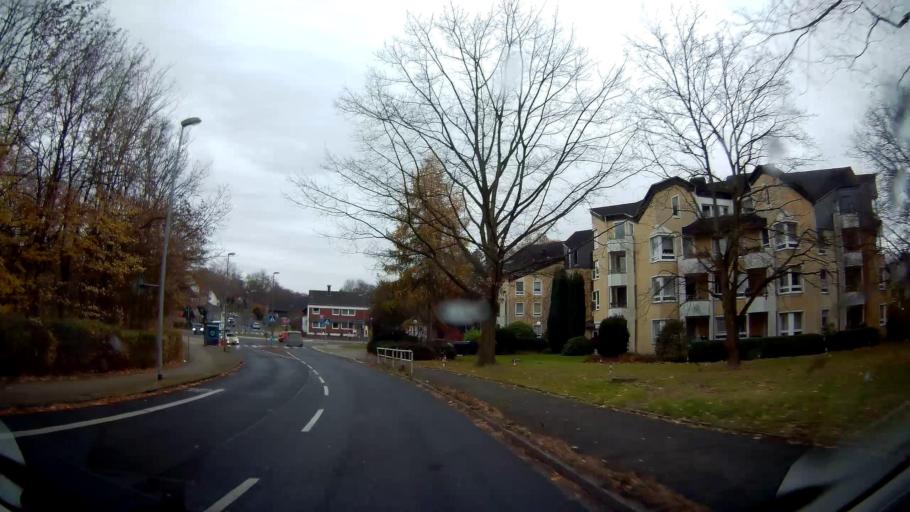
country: DE
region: North Rhine-Westphalia
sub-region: Regierungsbezirk Arnsberg
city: Bochum
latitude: 51.5008
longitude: 7.2284
